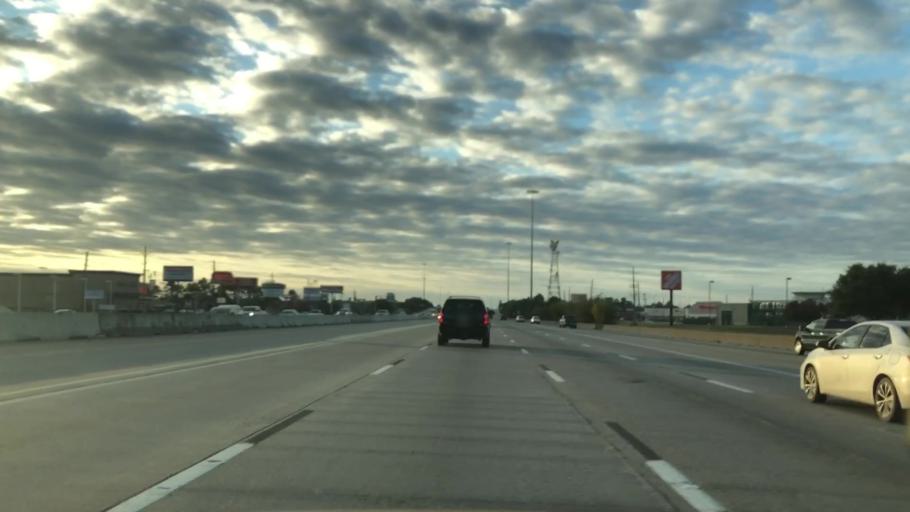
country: US
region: Texas
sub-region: Harris County
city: Spring
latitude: 30.0591
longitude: -95.4332
